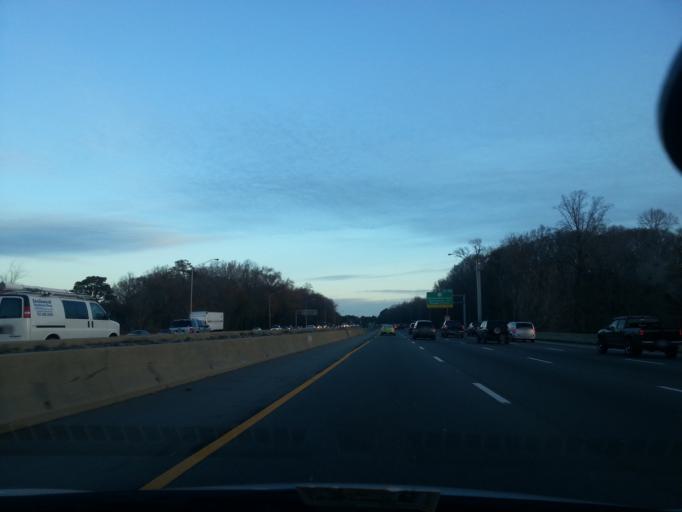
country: US
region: Virginia
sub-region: City of Chesapeake
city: Chesapeake
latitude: 36.8641
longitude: -76.1951
